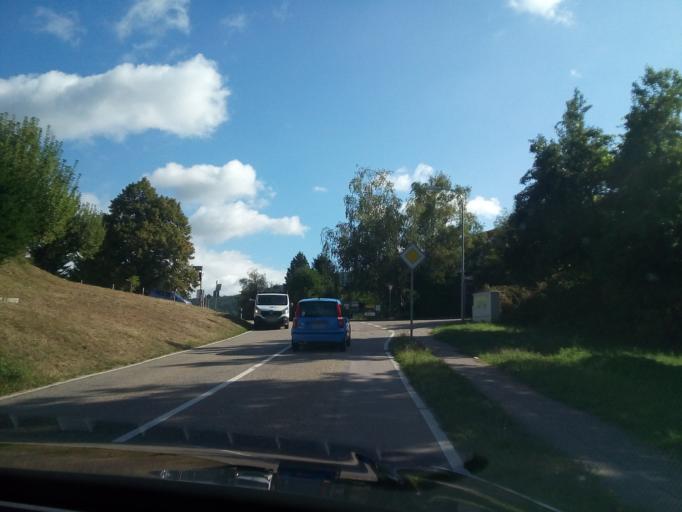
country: DE
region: Baden-Wuerttemberg
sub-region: Karlsruhe Region
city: Sinzheim
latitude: 48.7342
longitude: 8.1739
